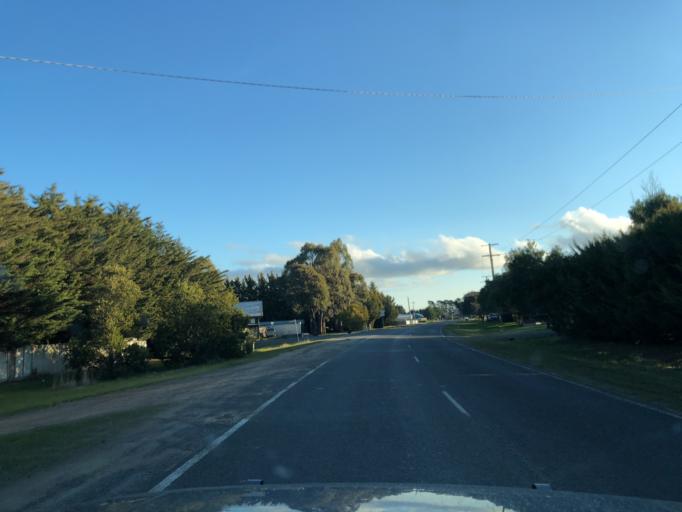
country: AU
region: Victoria
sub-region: Moorabool
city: Bacchus Marsh
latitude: -37.5927
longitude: 144.2351
